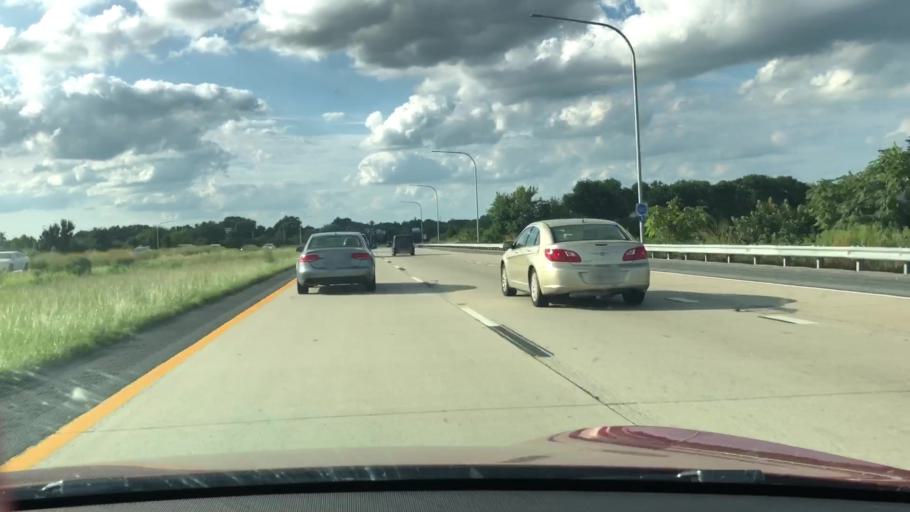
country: US
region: Delaware
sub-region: Kent County
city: Smyrna
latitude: 39.2833
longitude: -75.5891
